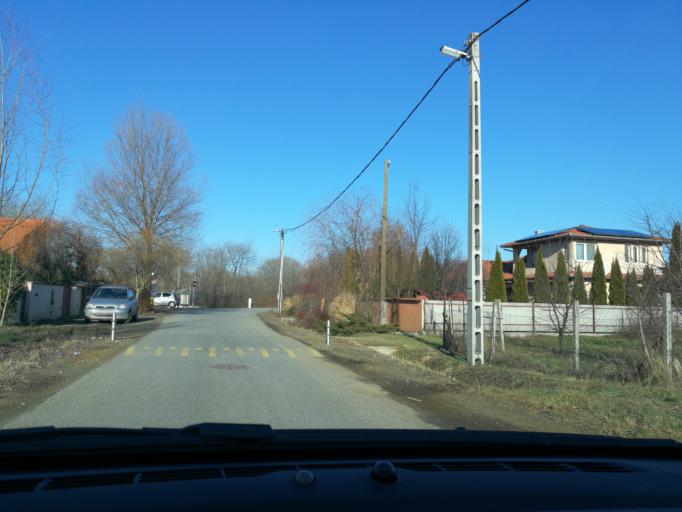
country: HU
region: Szabolcs-Szatmar-Bereg
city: Nyiregyhaza
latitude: 47.9485
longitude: 21.7472
